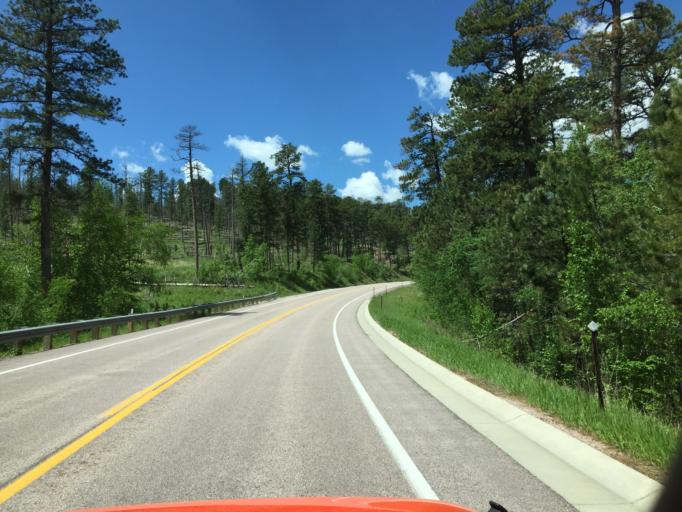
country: US
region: South Dakota
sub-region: Custer County
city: Custer
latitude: 43.8954
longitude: -103.5143
